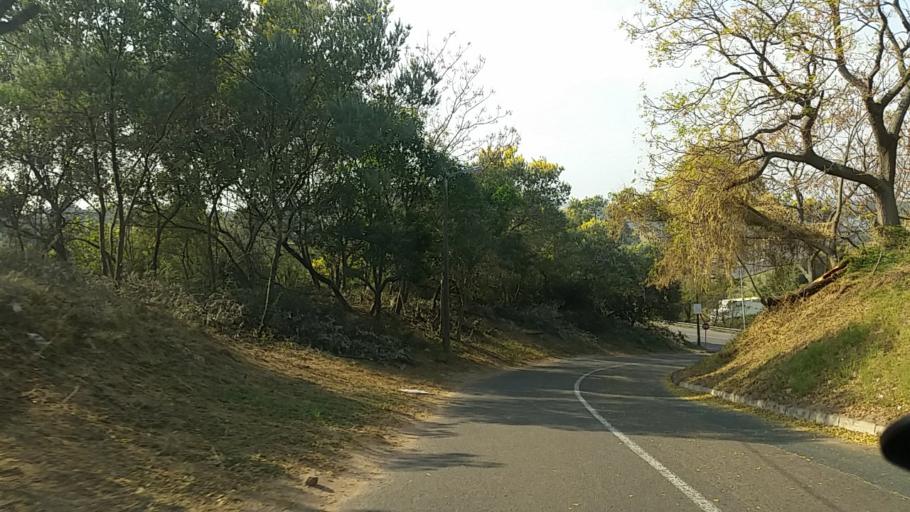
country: ZA
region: KwaZulu-Natal
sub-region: eThekwini Metropolitan Municipality
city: Berea
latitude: -29.8410
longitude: 30.9508
